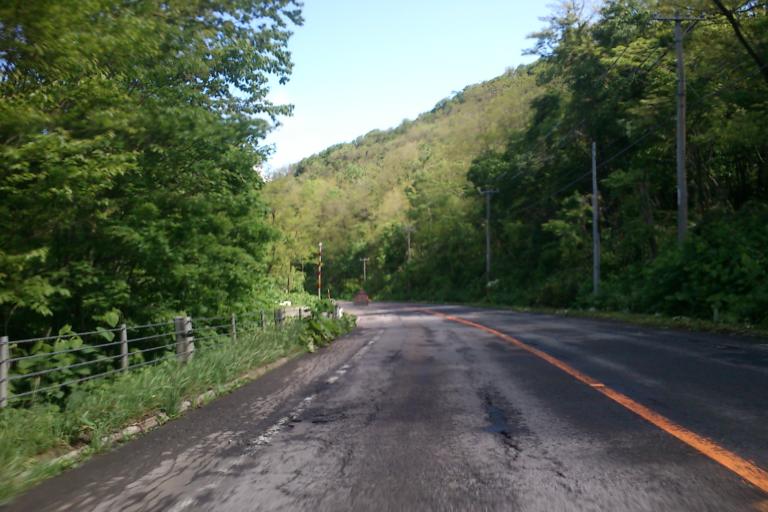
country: JP
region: Hokkaido
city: Ishikari
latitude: 43.5470
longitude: 141.3972
